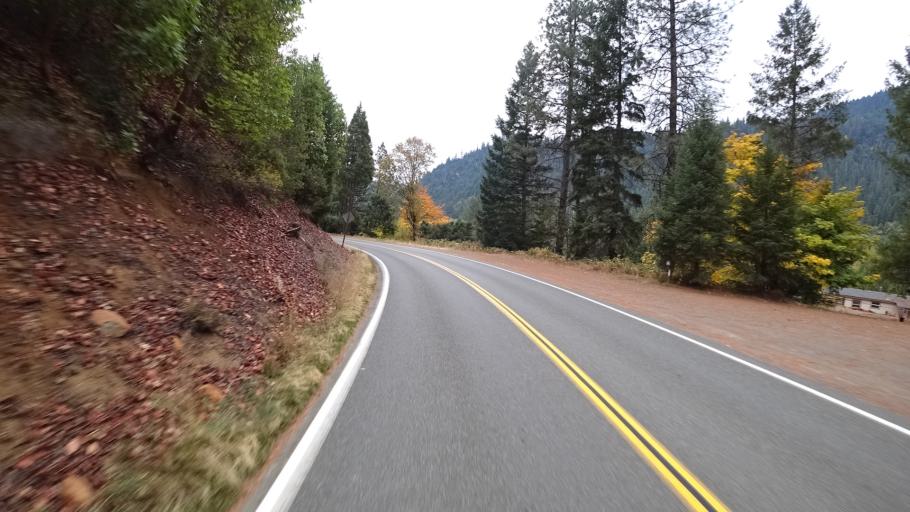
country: US
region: California
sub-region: Siskiyou County
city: Happy Camp
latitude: 41.8590
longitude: -123.4022
